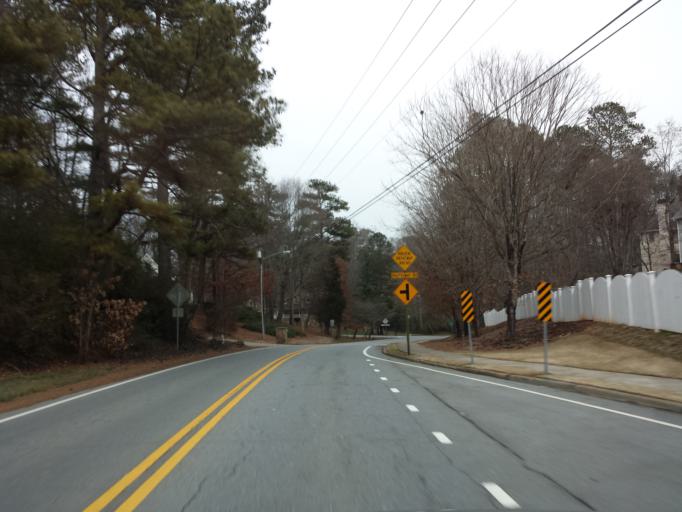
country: US
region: Georgia
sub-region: Fulton County
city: Roswell
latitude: 34.0162
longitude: -84.3832
